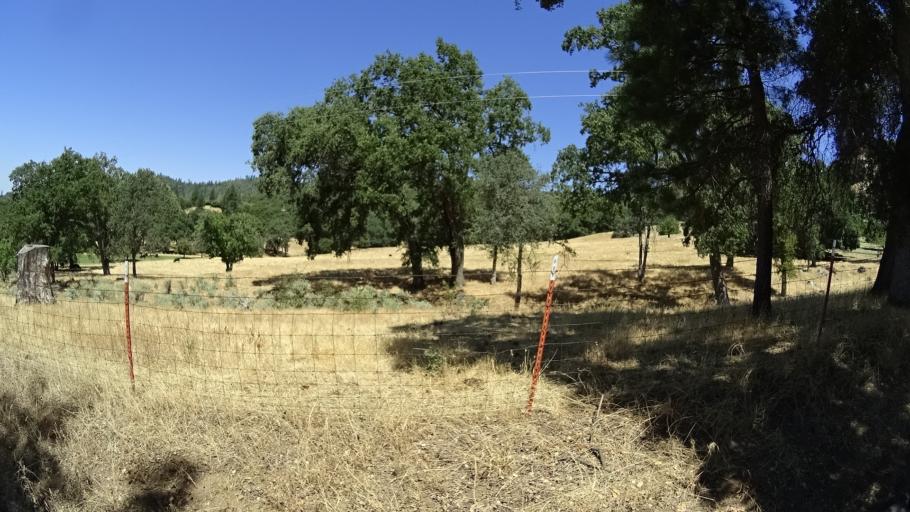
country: US
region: California
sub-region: Calaveras County
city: Forest Meadows
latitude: 38.1372
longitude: -120.4071
